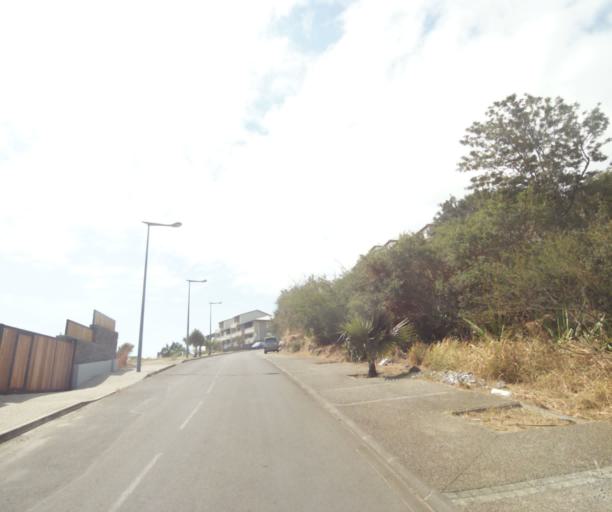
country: RE
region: Reunion
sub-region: Reunion
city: Saint-Paul
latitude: -21.0475
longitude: 55.2599
